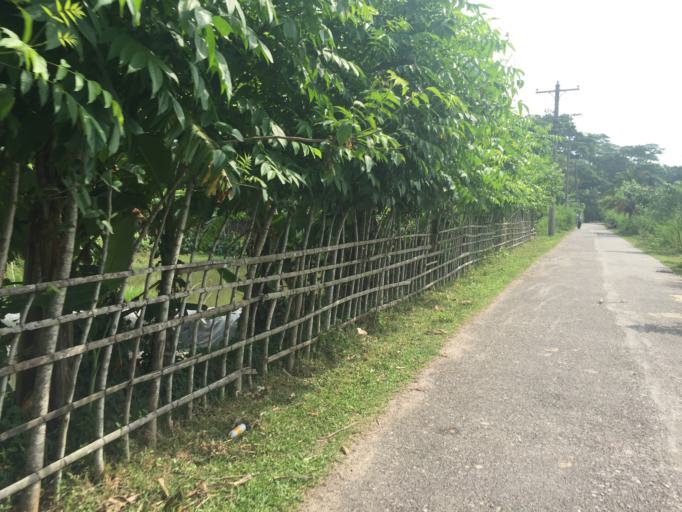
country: BD
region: Barisal
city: Mathba
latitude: 22.2494
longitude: 89.9140
